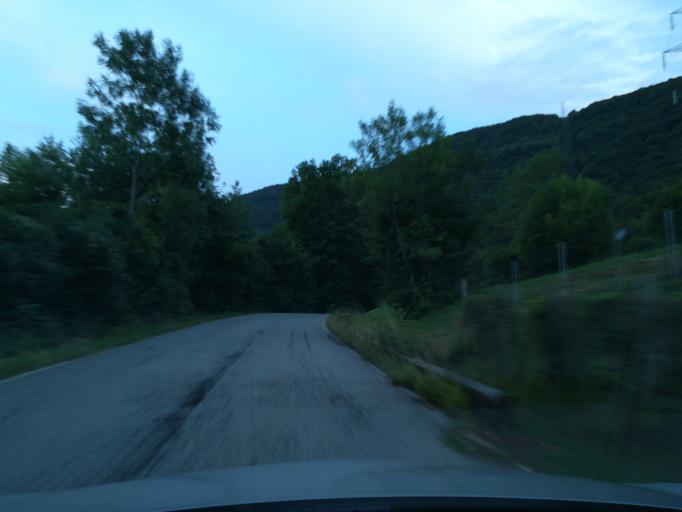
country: IT
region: Lombardy
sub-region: Provincia di Bergamo
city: Valsecca
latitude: 45.8220
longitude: 9.4872
